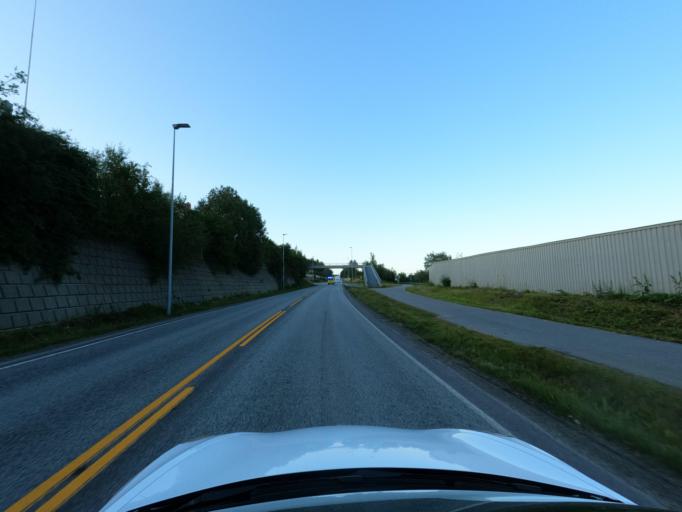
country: NO
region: Troms
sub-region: Harstad
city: Harstad
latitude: 68.7482
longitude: 16.5591
